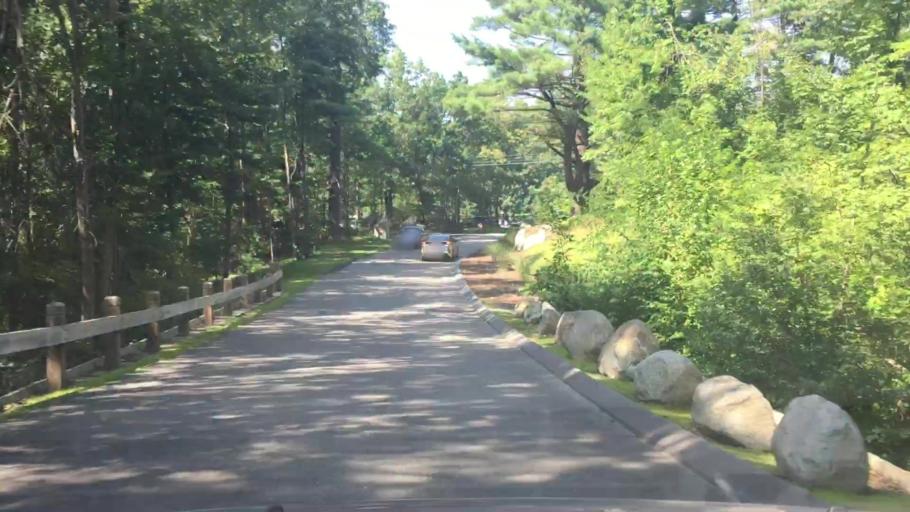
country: US
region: Massachusetts
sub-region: Middlesex County
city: Littleton Common
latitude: 42.5492
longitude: -71.4621
